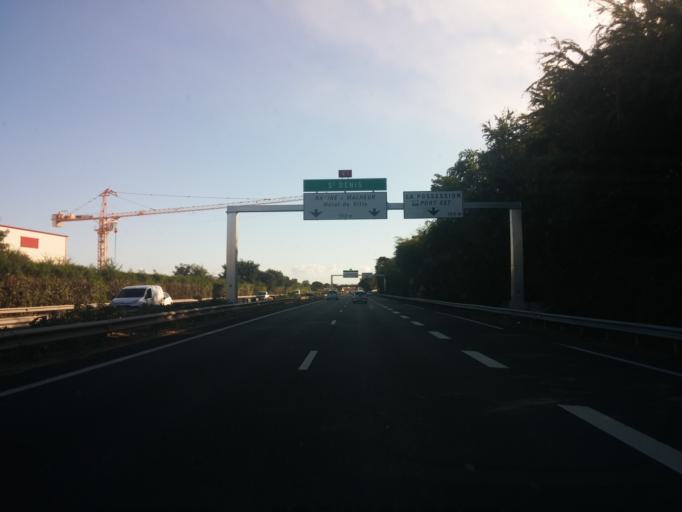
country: RE
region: Reunion
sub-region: Reunion
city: La Possession
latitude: -20.9343
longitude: 55.3308
